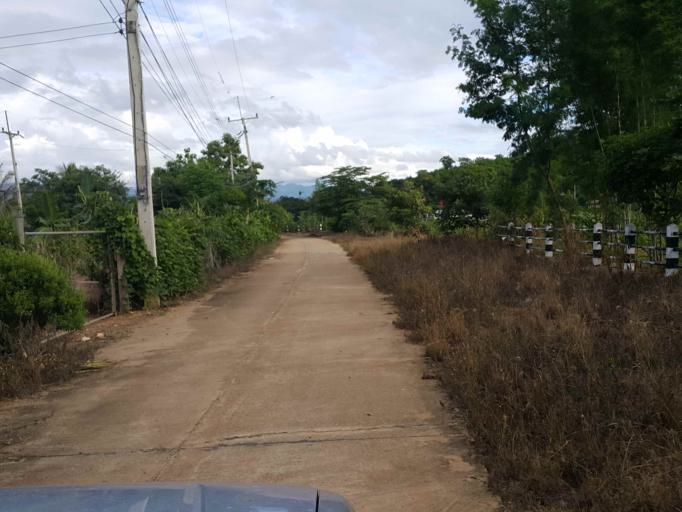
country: TH
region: Chiang Mai
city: Mae Chaem
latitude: 18.4950
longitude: 98.3618
